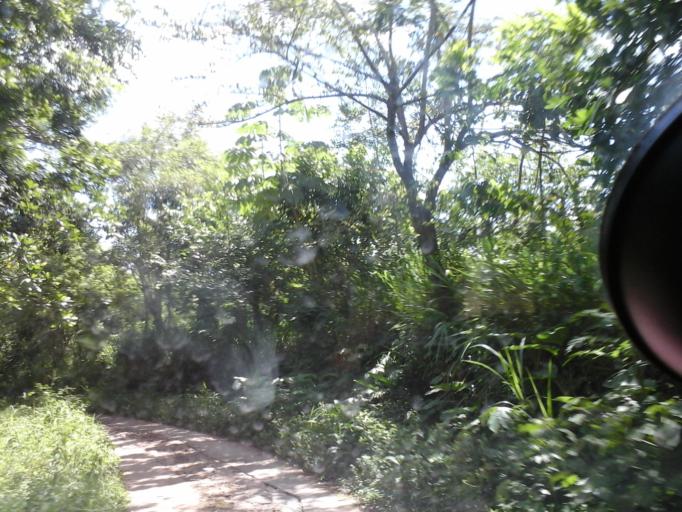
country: CO
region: Cesar
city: San Diego
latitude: 10.2719
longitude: -73.0918
